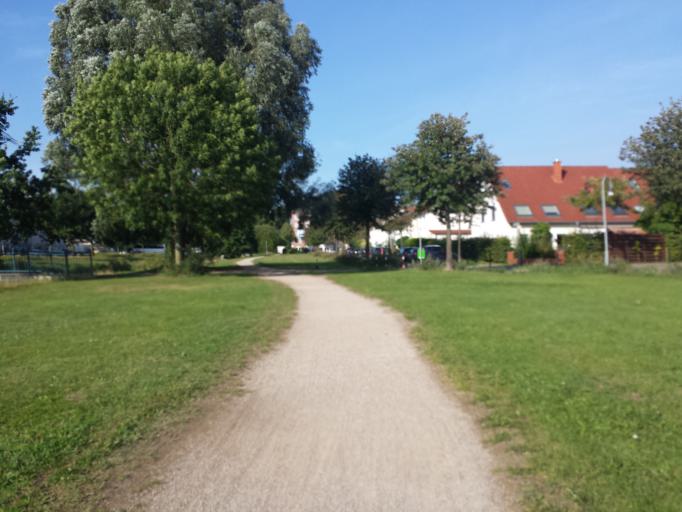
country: DE
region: Bremen
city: Bremen
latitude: 53.0310
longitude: 8.8342
